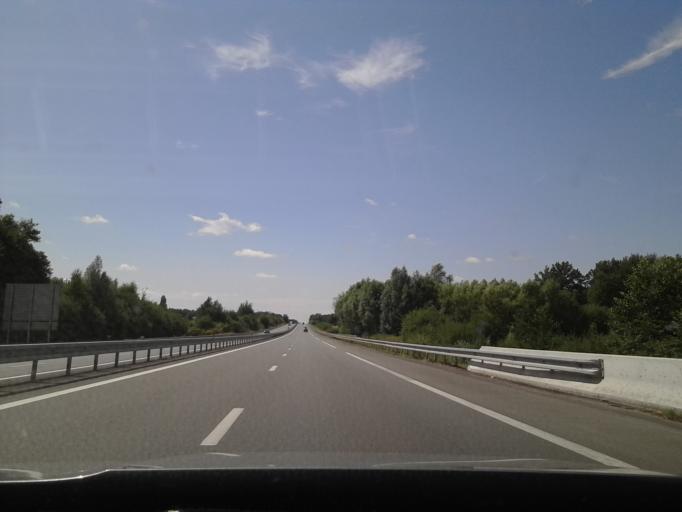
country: FR
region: Pays de la Loire
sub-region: Departement de la Sarthe
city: Champagne
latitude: 47.9740
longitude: 0.3300
